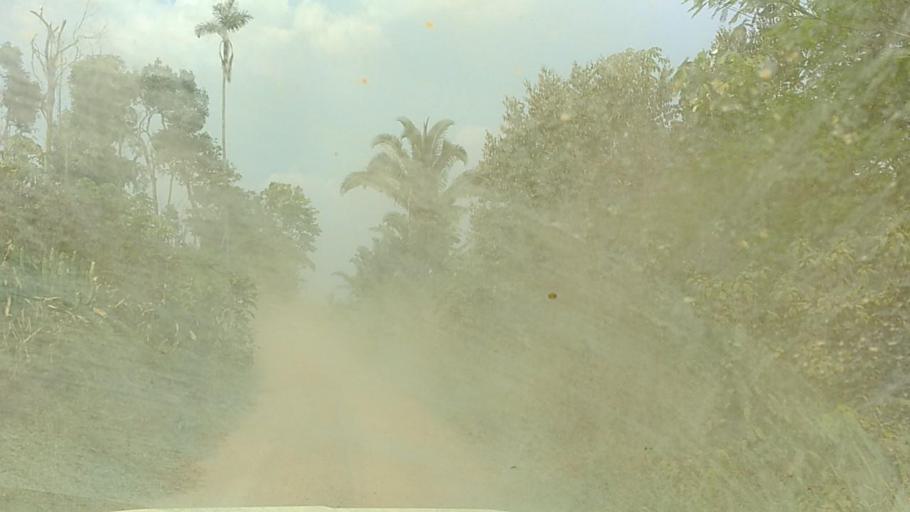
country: BR
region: Rondonia
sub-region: Porto Velho
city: Porto Velho
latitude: -8.7730
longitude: -63.1971
